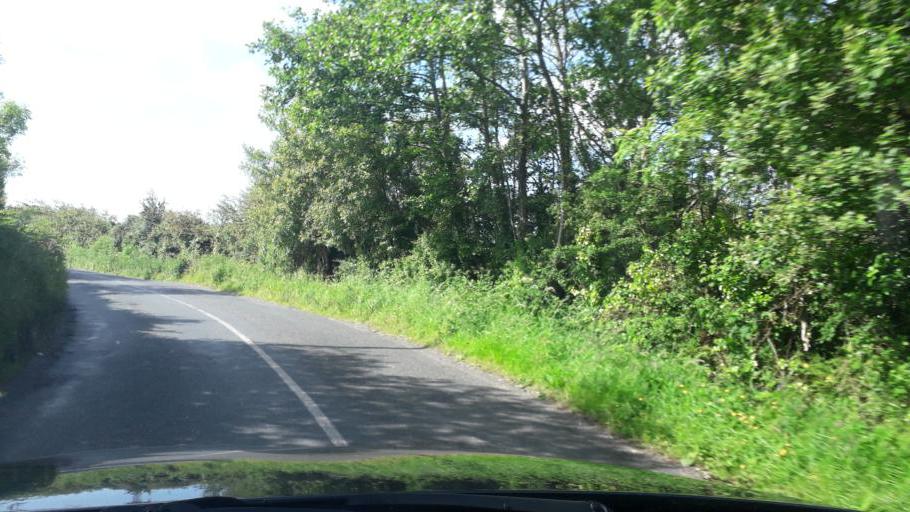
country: IE
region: Leinster
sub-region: Loch Garman
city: Loch Garman
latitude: 52.2534
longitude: -6.5518
